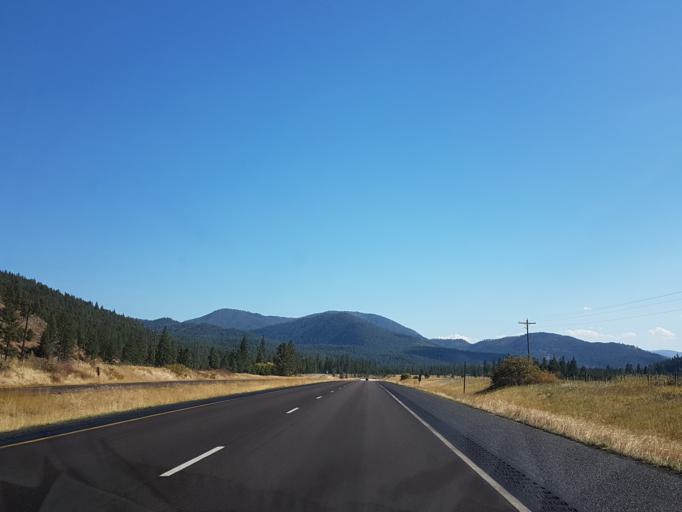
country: US
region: Montana
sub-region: Mineral County
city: Superior
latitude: 47.1389
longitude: -114.8073
